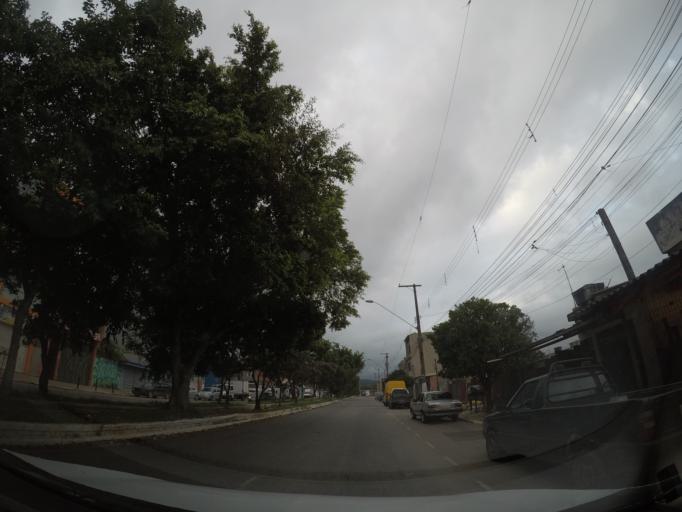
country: BR
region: Sao Paulo
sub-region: Aruja
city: Aruja
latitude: -23.3980
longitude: -46.4197
